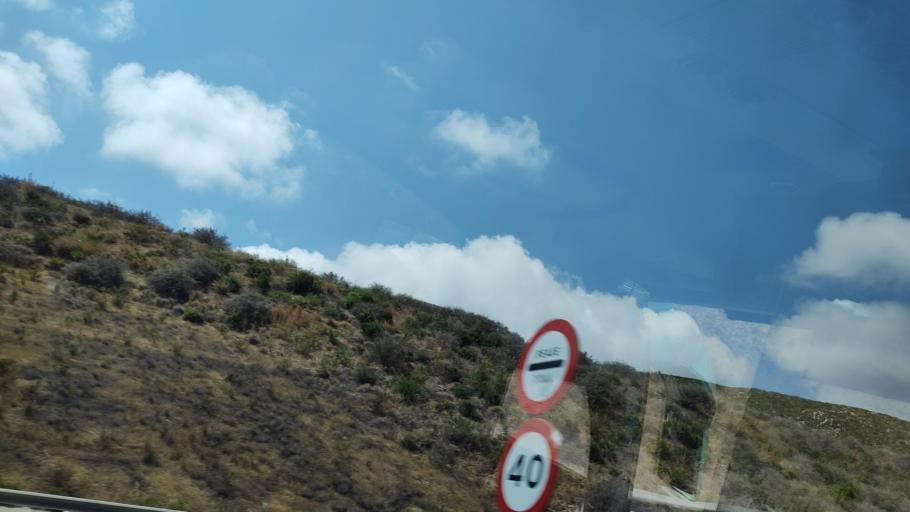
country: ES
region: Andalusia
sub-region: Provincia de Malaga
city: Manilva
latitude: 36.3730
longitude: -5.2674
